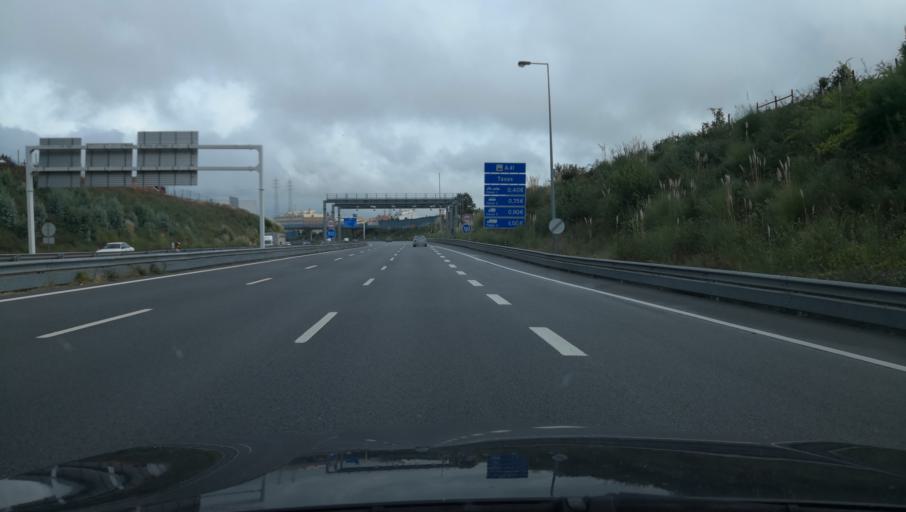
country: PT
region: Porto
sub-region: Maia
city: Maia
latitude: 41.2401
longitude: -8.6196
